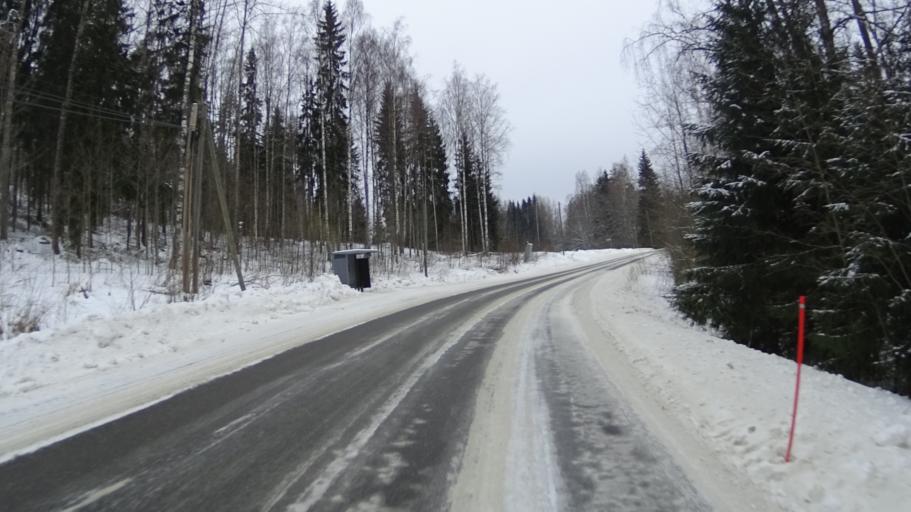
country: FI
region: Uusimaa
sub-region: Helsinki
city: Karkkila
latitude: 60.4990
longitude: 24.1379
